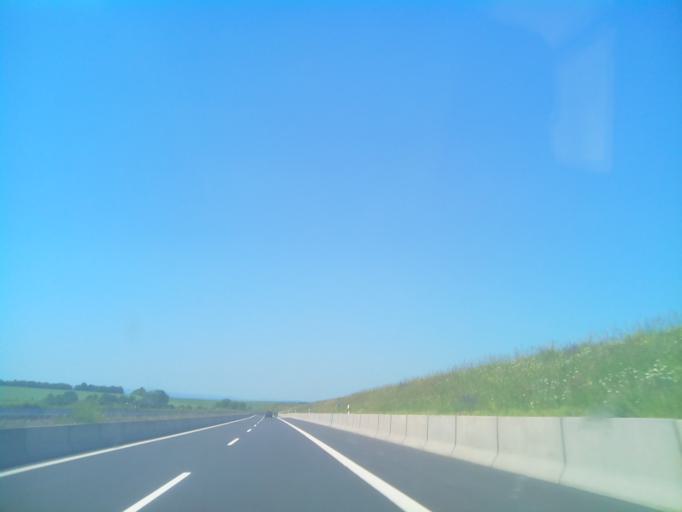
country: DE
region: Bavaria
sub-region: Regierungsbezirk Unterfranken
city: Munnerstadt
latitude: 50.2136
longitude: 10.2199
